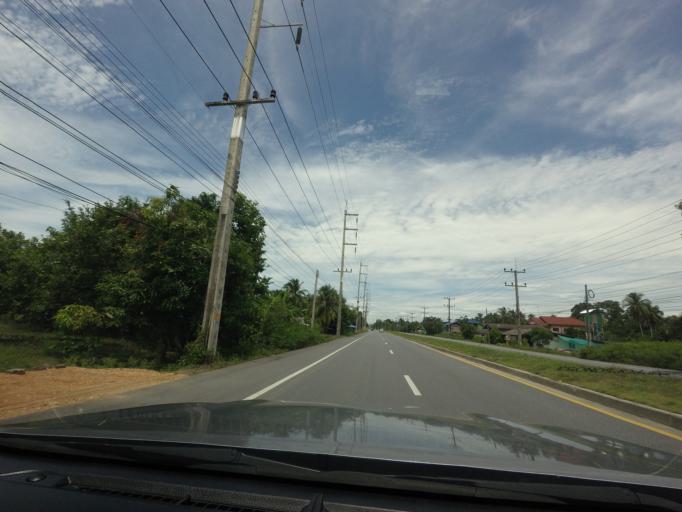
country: TH
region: Songkhla
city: Krasae Sin
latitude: 7.6075
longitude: 100.3994
